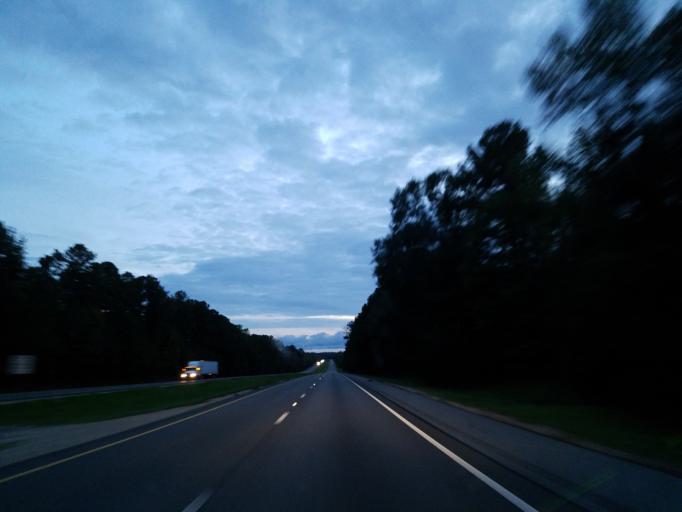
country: US
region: Mississippi
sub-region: Clarke County
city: Stonewall
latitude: 32.1159
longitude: -88.8805
